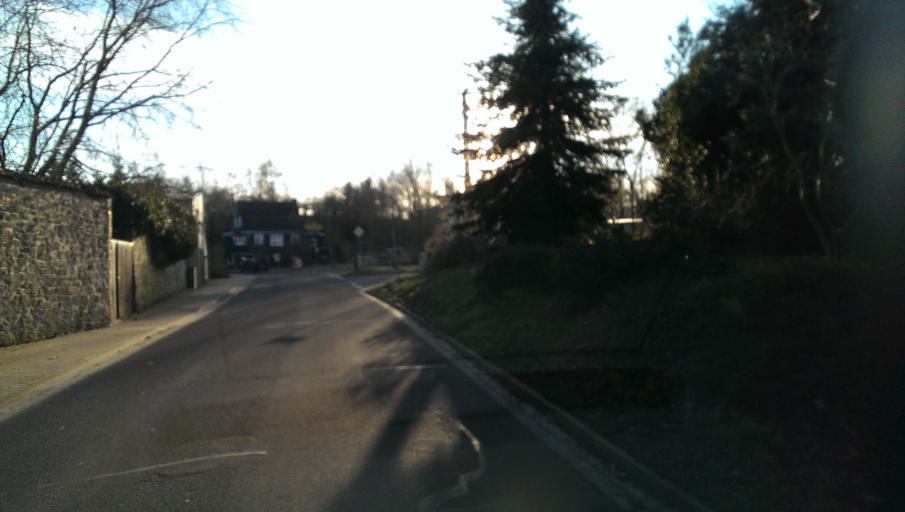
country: DE
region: Saxony-Anhalt
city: Eilsleben
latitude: 52.1321
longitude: 11.1910
